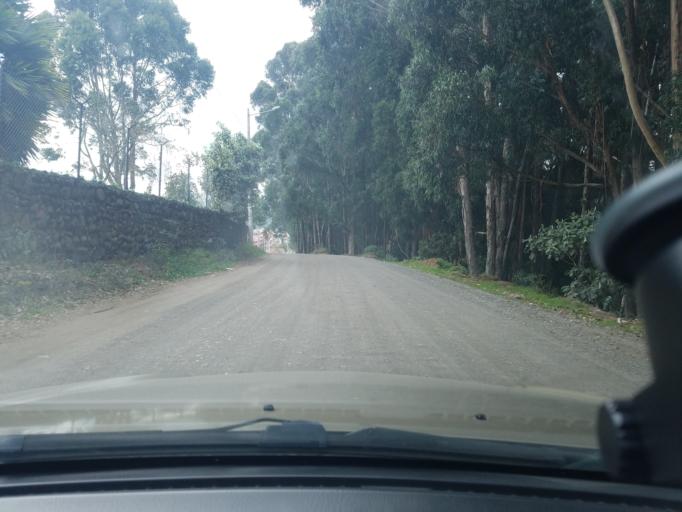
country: EC
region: Azuay
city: Cuenca
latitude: -2.9095
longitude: -79.0162
